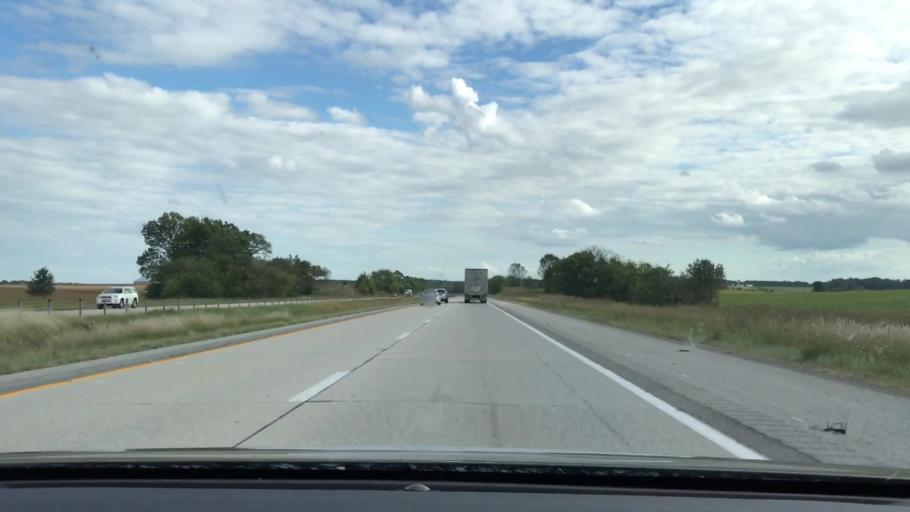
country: US
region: Kentucky
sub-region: Trigg County
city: Cadiz
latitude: 36.8649
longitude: -87.7102
